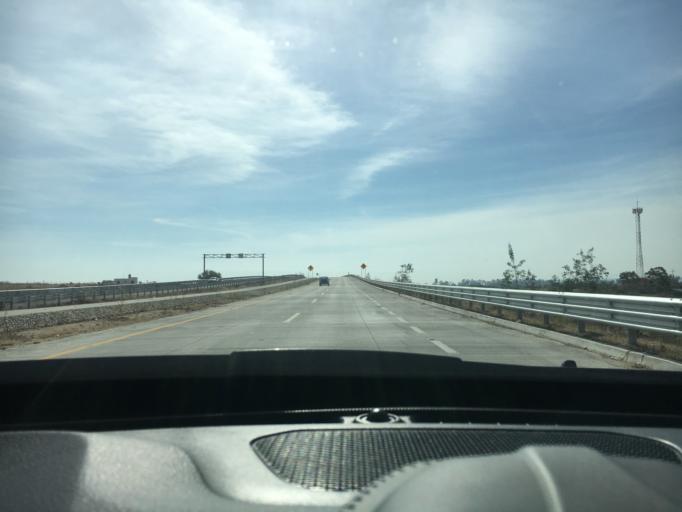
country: MX
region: Guanajuato
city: Duarte
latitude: 21.0542
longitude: -101.5306
